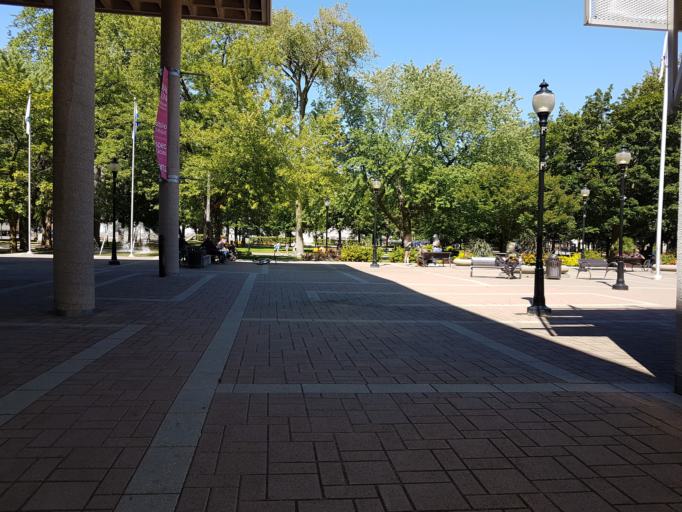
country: CA
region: Quebec
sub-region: Mauricie
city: Trois-Rivieres
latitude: 46.3431
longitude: -72.5431
